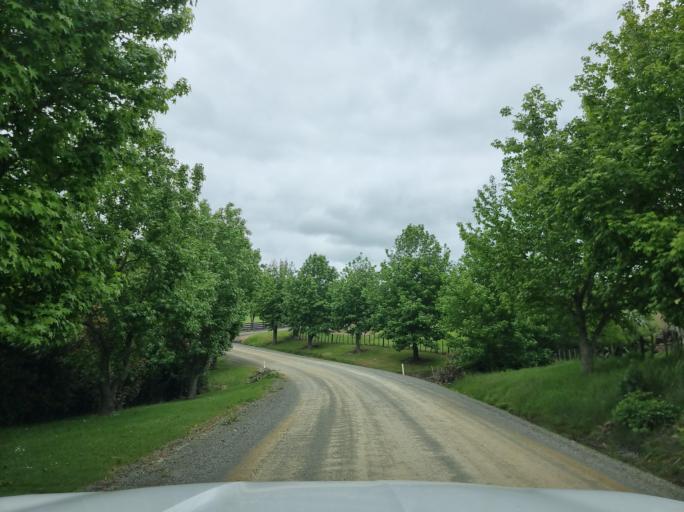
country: NZ
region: Auckland
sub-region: Auckland
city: Wellsford
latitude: -36.0919
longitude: 174.5296
